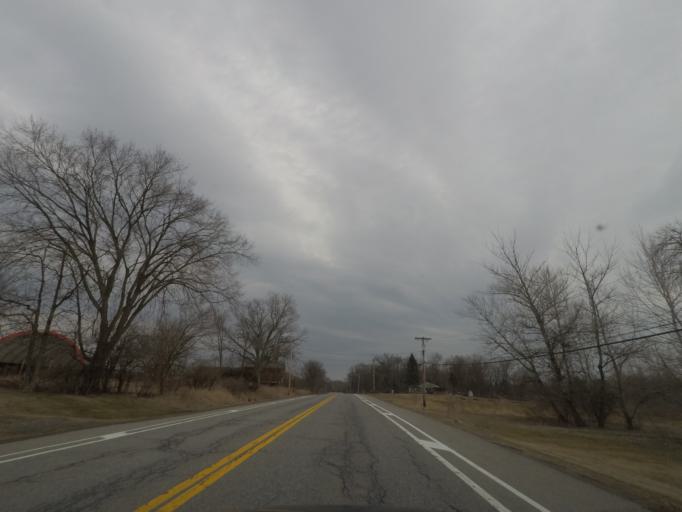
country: US
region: New York
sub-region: Washington County
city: Fort Edward
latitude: 43.2347
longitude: -73.5903
